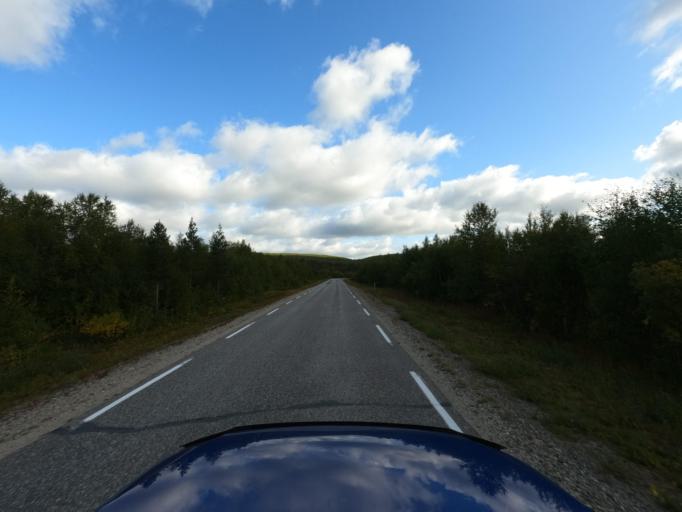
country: NO
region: Finnmark Fylke
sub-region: Porsanger
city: Lakselv
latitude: 69.4286
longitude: 24.8801
